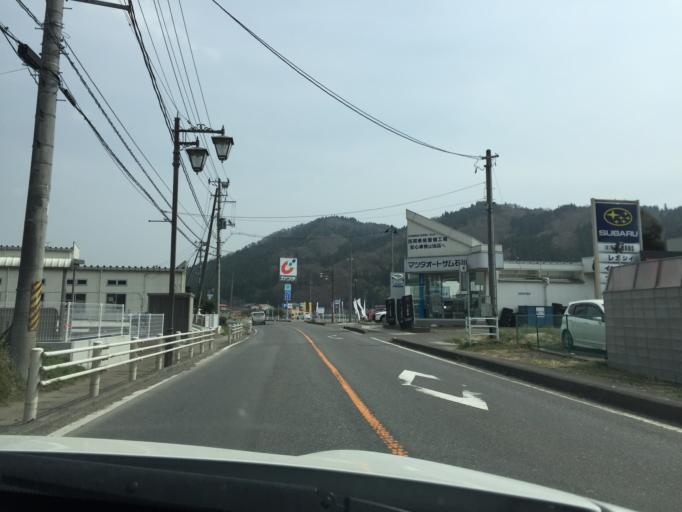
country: JP
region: Fukushima
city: Ishikawa
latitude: 37.1478
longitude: 140.4709
